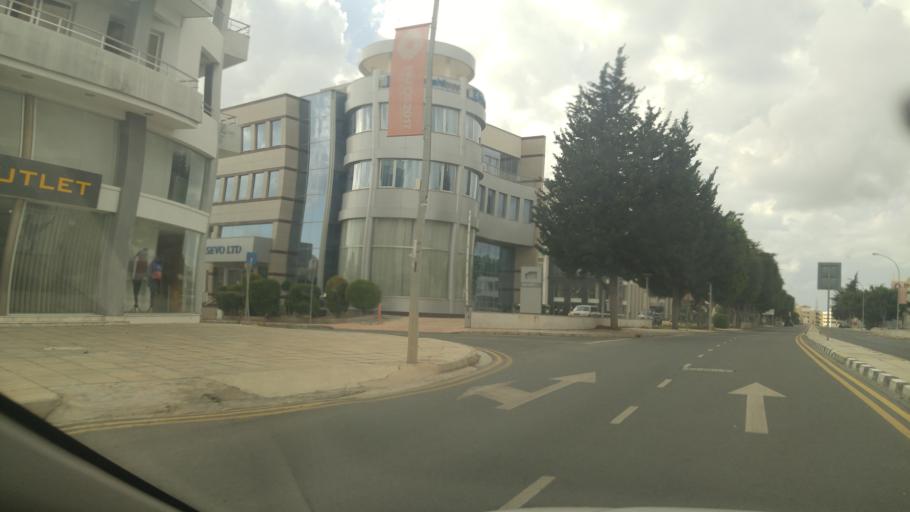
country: CY
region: Pafos
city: Paphos
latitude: 34.7684
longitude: 32.4384
